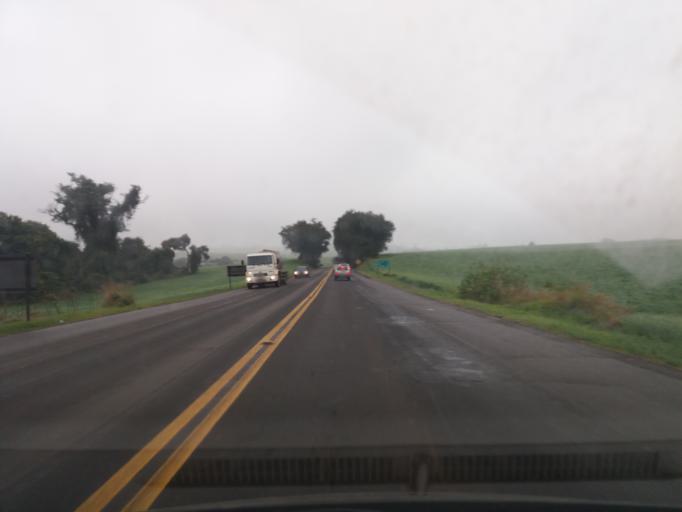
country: BR
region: Parana
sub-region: Realeza
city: Realeza
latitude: -25.8071
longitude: -53.5216
